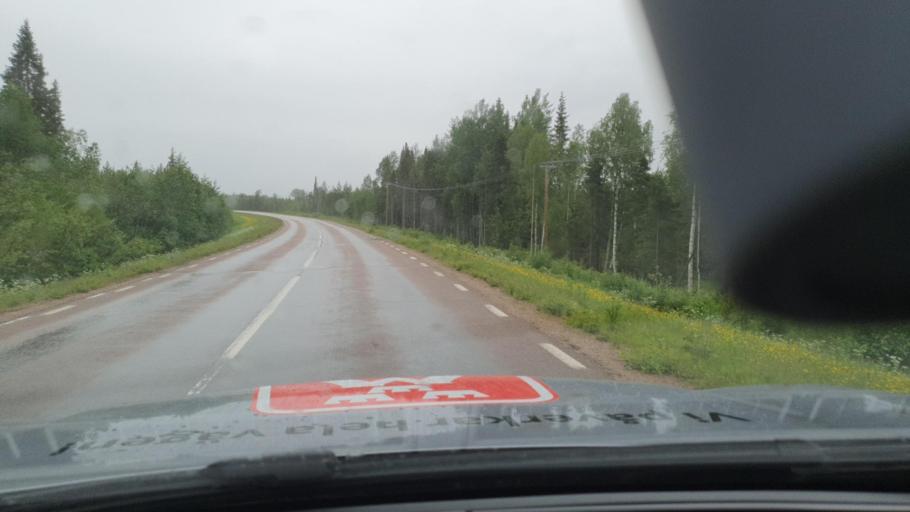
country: SE
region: Norrbotten
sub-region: Overtornea Kommun
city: OEvertornea
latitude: 66.4504
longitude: 23.2989
